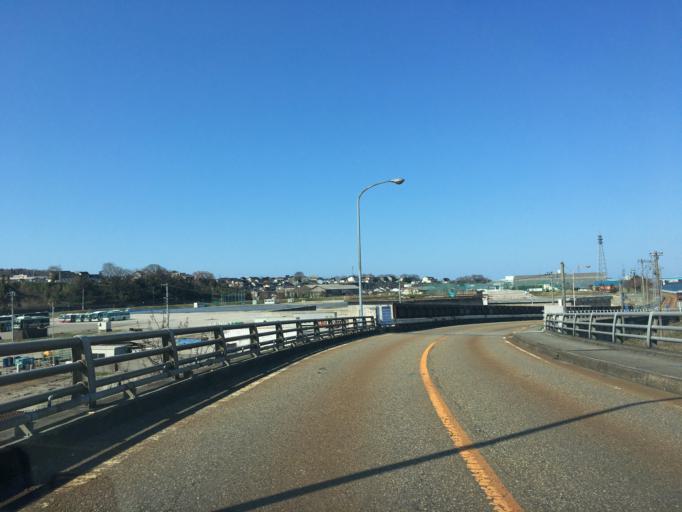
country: JP
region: Toyama
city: Nishishinminato
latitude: 36.7814
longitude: 137.0486
